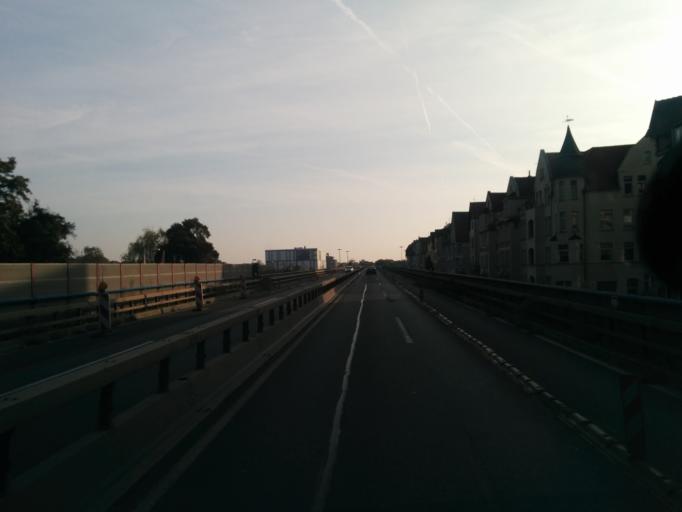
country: DE
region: Lower Saxony
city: Hannover
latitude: 52.3417
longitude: 9.7599
